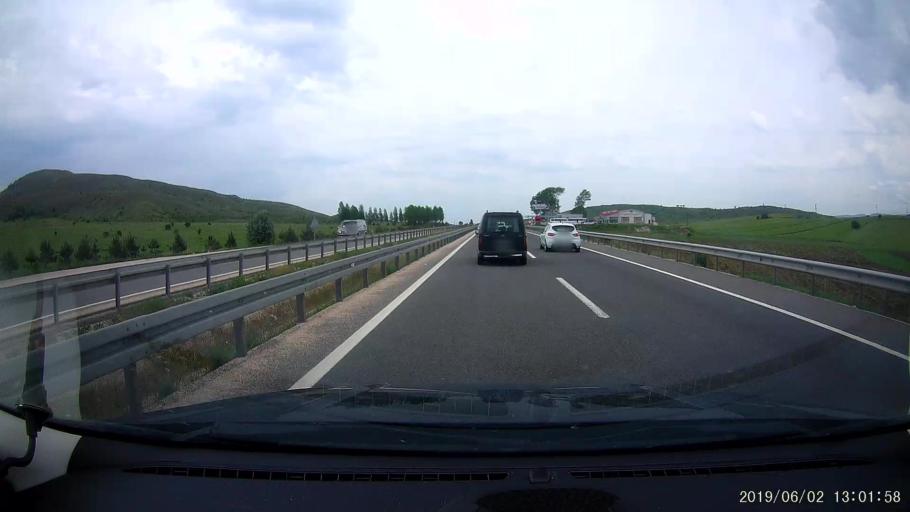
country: TR
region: Karabuk
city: Gozyeri
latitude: 40.8533
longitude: 32.4731
